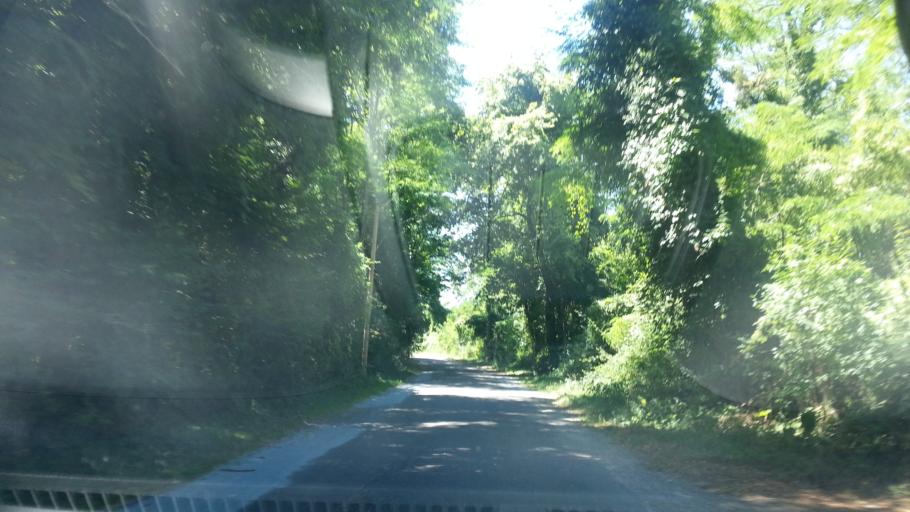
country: FR
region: Aquitaine
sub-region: Departement de la Gironde
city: Landiras
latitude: 44.5670
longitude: -0.4006
